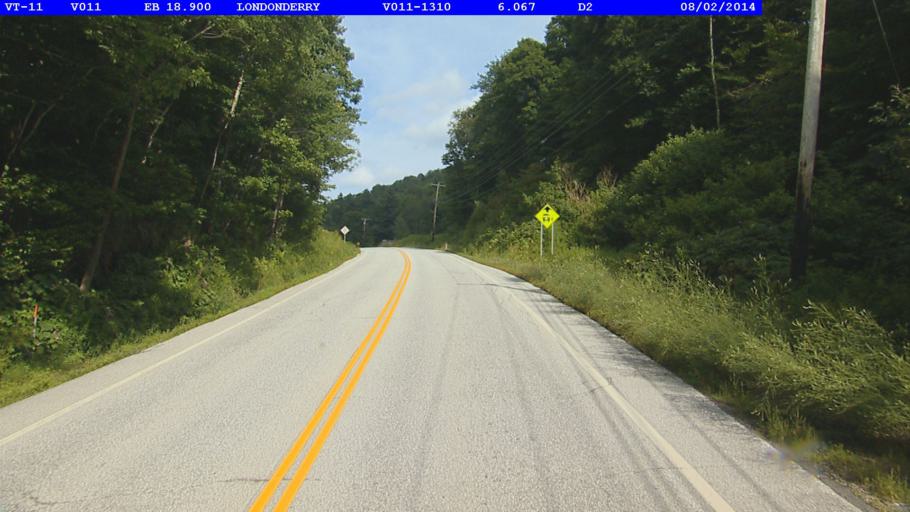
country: US
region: Vermont
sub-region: Windsor County
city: Chester
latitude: 43.2143
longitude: -72.7497
